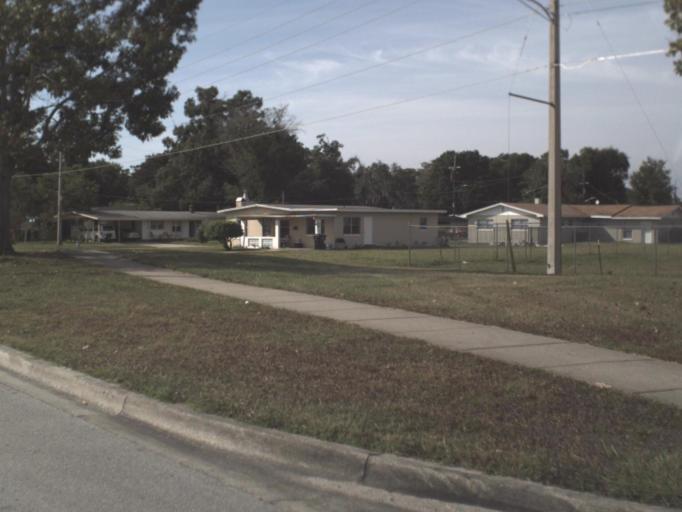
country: US
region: Florida
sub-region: Orange County
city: Orlando
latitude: 28.5378
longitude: -81.4137
